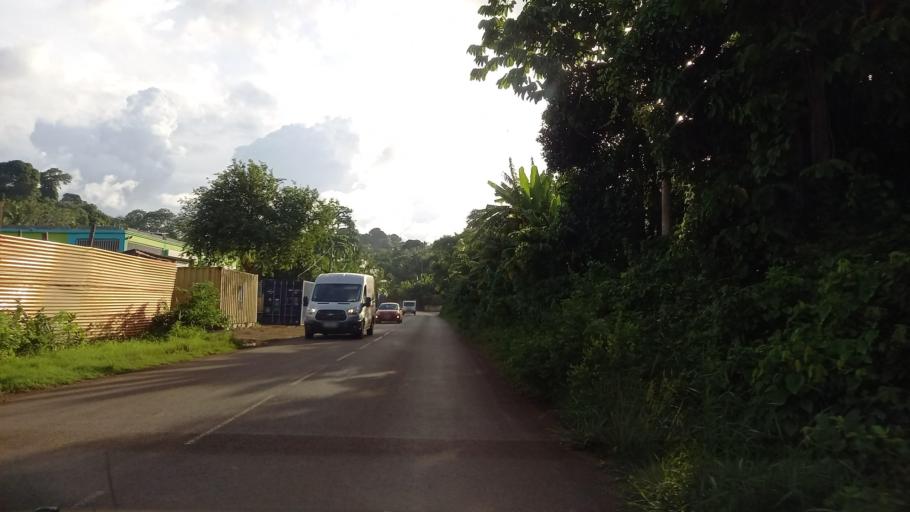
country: YT
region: Bandraboua
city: Bandraboua
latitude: -12.7261
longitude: 45.1222
